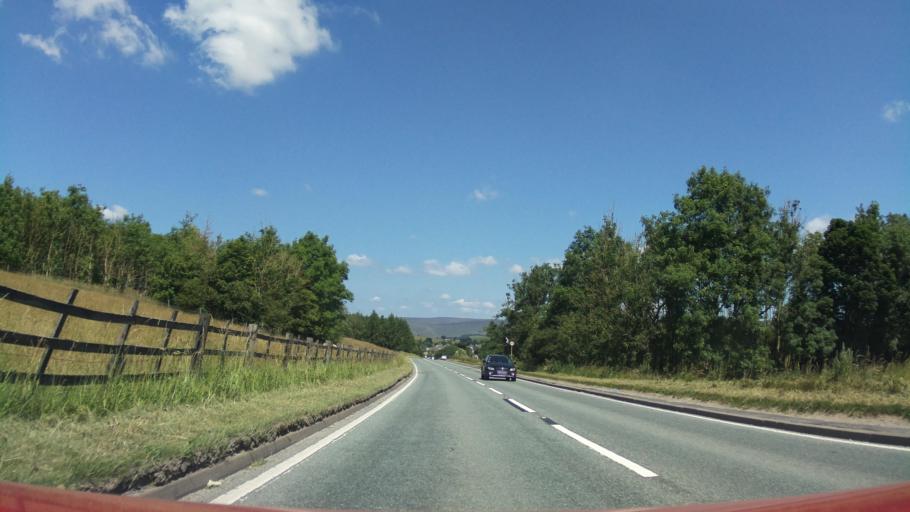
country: GB
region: England
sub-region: Derbyshire
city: Buxton
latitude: 53.2888
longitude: -1.8894
